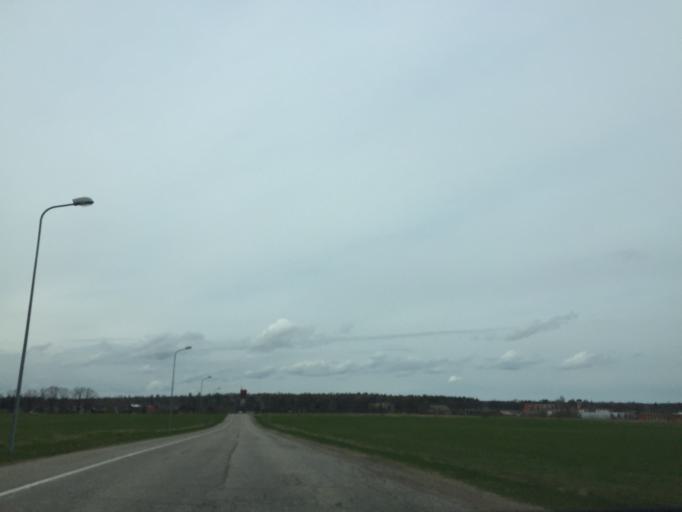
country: LV
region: Priekuli
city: Priekuli
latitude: 57.3448
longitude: 25.3380
